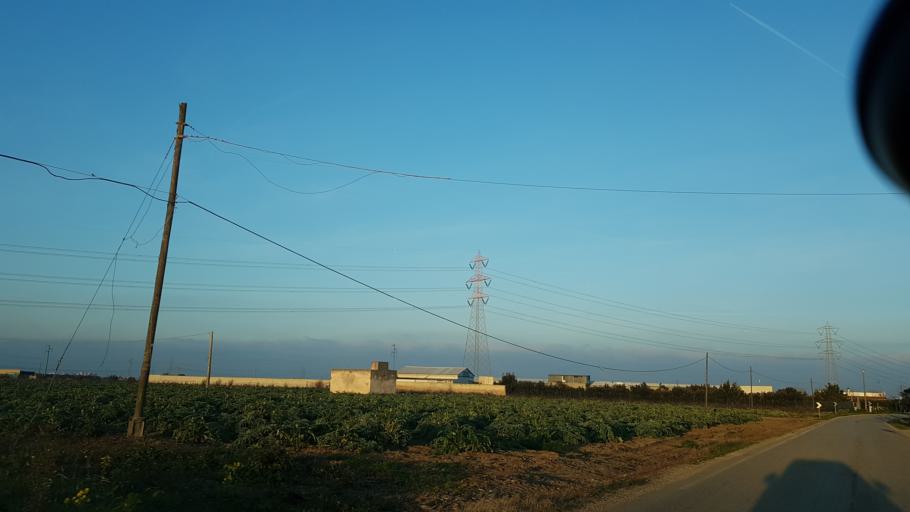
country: IT
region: Apulia
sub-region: Provincia di Brindisi
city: La Rosa
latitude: 40.5912
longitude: 17.9370
